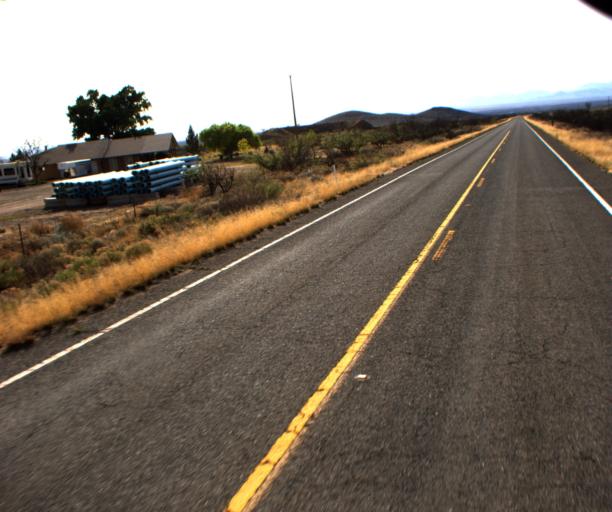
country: US
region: Arizona
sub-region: Cochise County
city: Willcox
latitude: 32.1825
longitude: -109.6636
